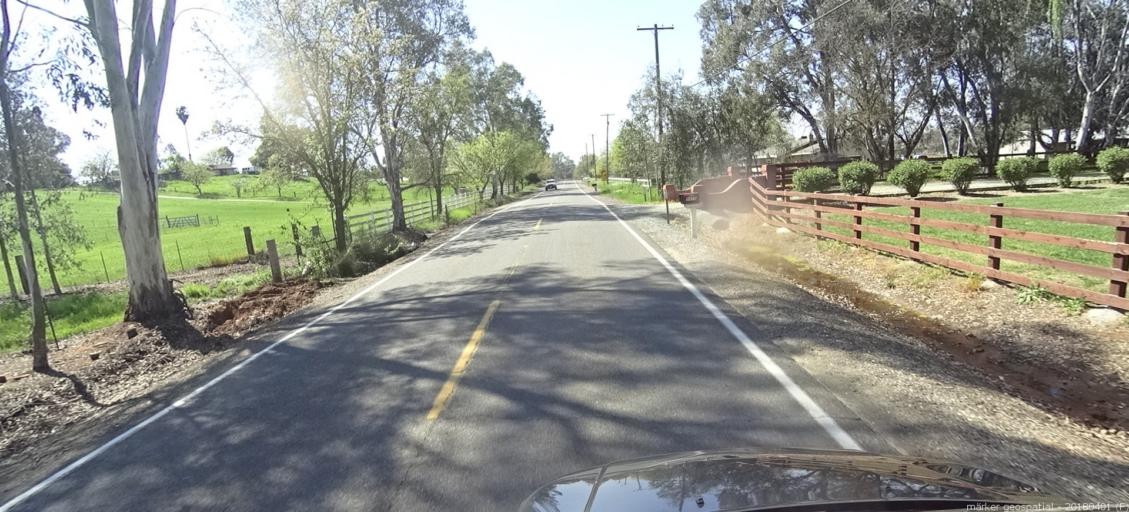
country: US
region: California
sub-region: Sacramento County
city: Wilton
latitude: 38.4087
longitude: -121.2390
